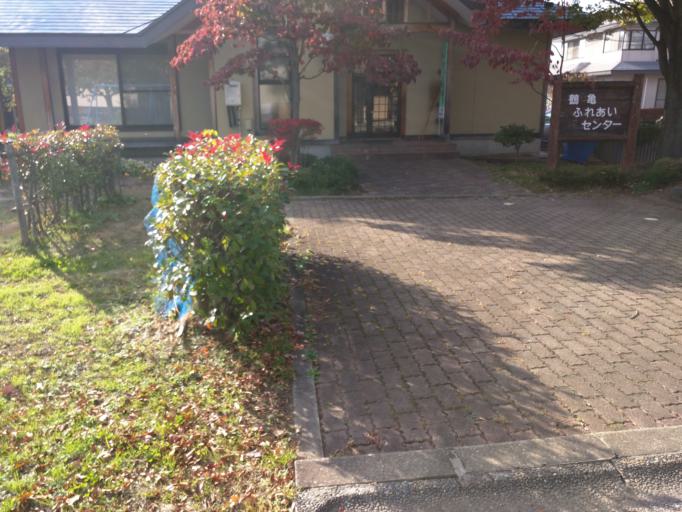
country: JP
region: Fukushima
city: Kitakata
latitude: 37.5199
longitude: 139.9383
